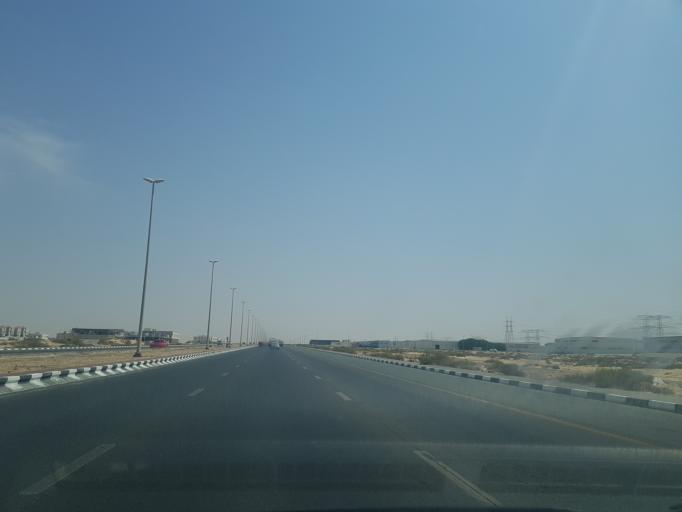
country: AE
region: Ash Shariqah
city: Sharjah
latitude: 25.2546
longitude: 55.5234
